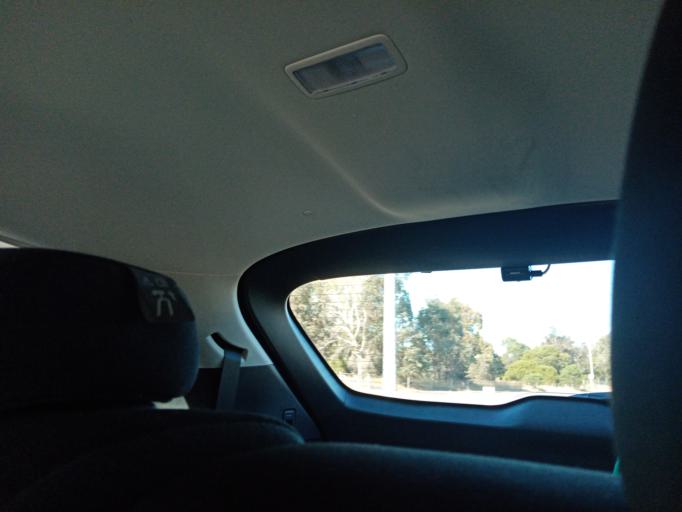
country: AU
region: Western Australia
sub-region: City of Cockburn
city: South Lake
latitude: -32.1252
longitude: 115.8336
